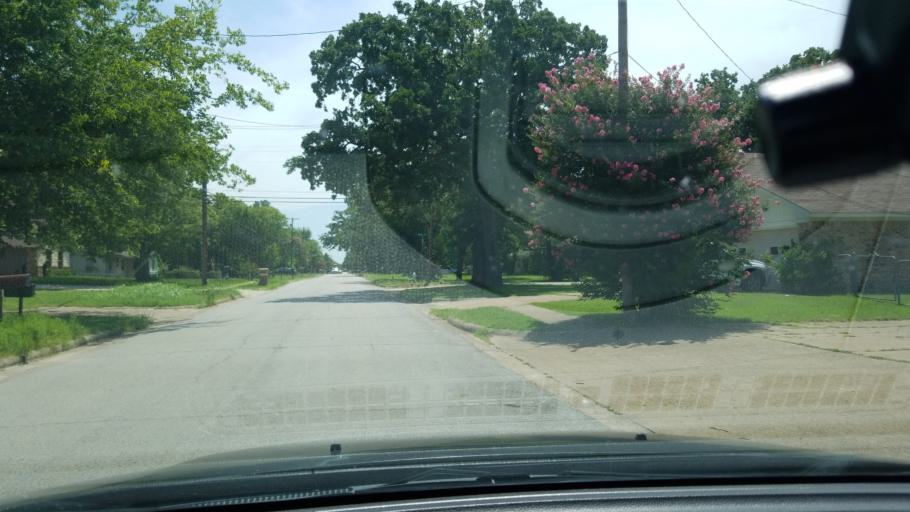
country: US
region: Texas
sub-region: Dallas County
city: Balch Springs
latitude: 32.7524
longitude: -96.6300
